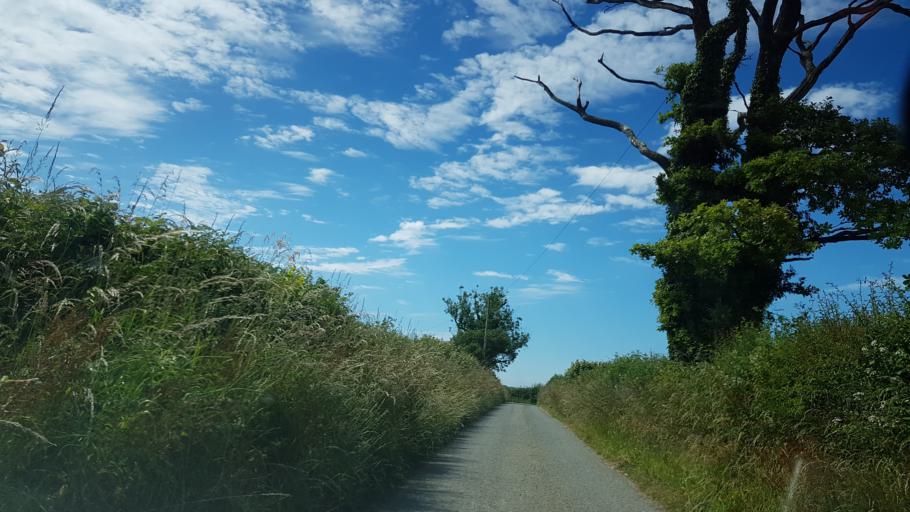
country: GB
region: Wales
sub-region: Pembrokeshire
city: Wiston
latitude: 51.8241
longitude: -4.9119
